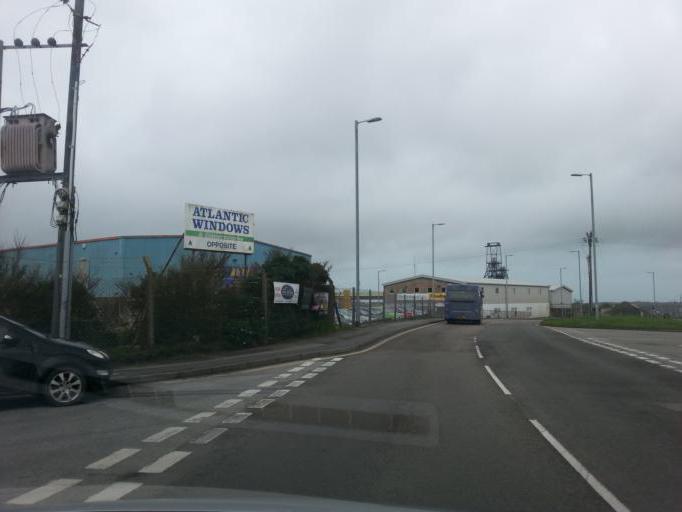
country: GB
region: England
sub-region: Cornwall
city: Camborne
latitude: 50.2211
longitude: -5.2716
